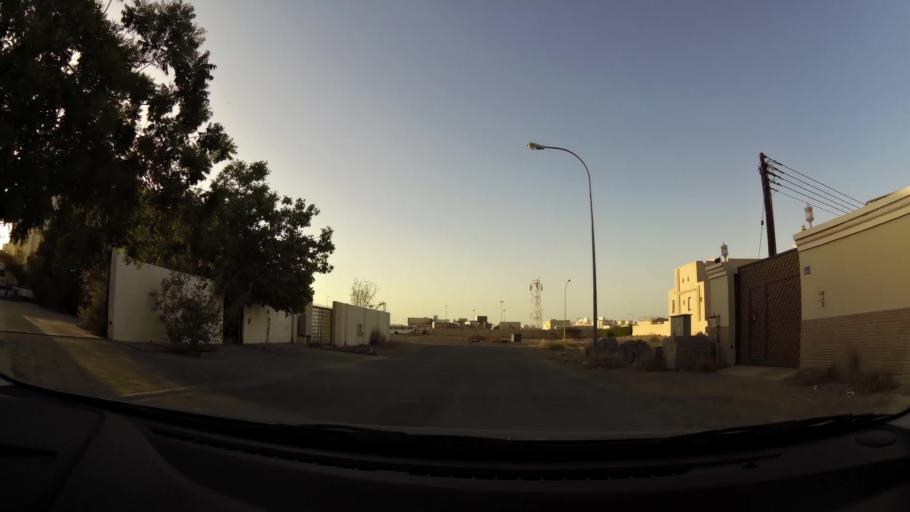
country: OM
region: Muhafazat Masqat
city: As Sib al Jadidah
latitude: 23.5996
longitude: 58.2184
